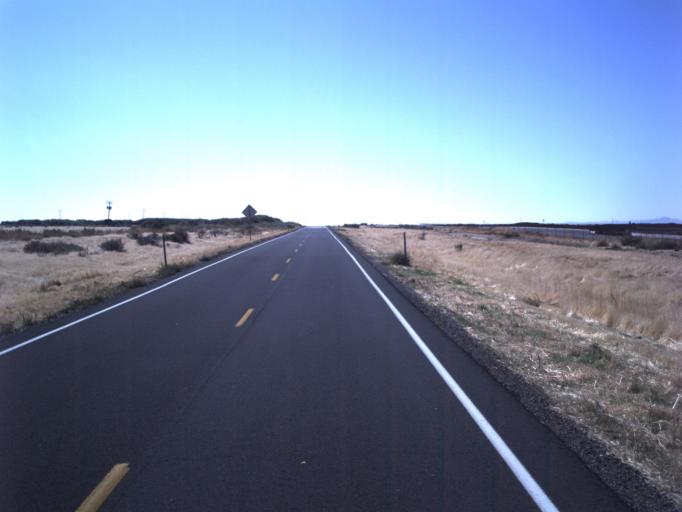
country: US
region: Utah
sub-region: Tooele County
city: Grantsville
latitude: 40.5322
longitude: -112.7477
